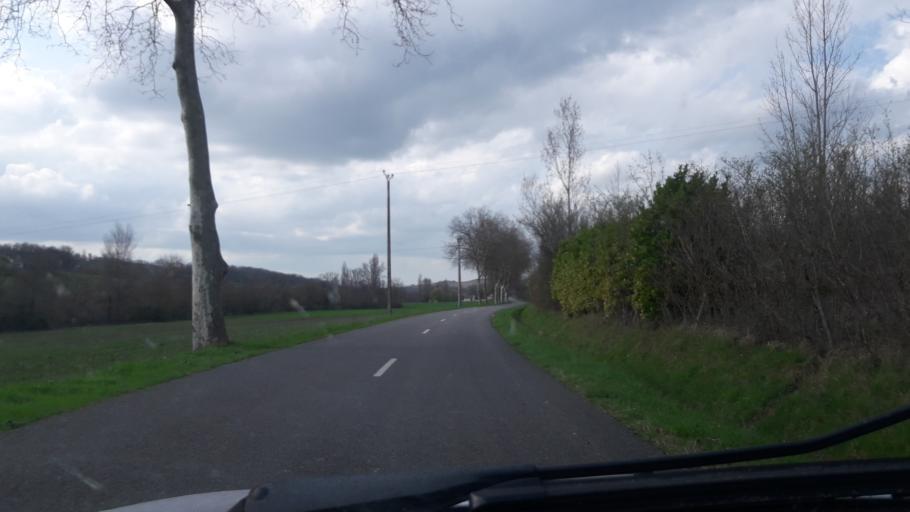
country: FR
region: Midi-Pyrenees
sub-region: Departement de la Haute-Garonne
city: Montesquieu-Volvestre
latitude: 43.2456
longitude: 1.2588
